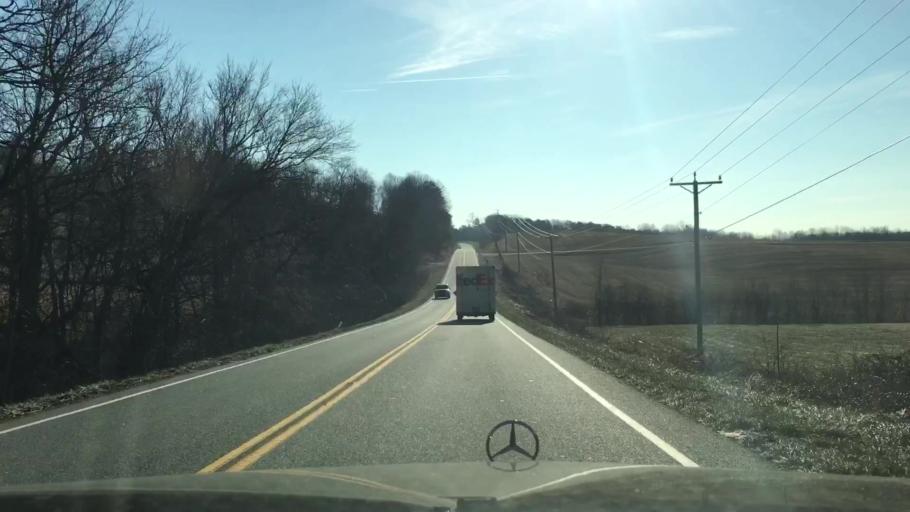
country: US
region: Virginia
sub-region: Franklin County
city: North Shore
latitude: 37.2474
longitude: -79.6867
